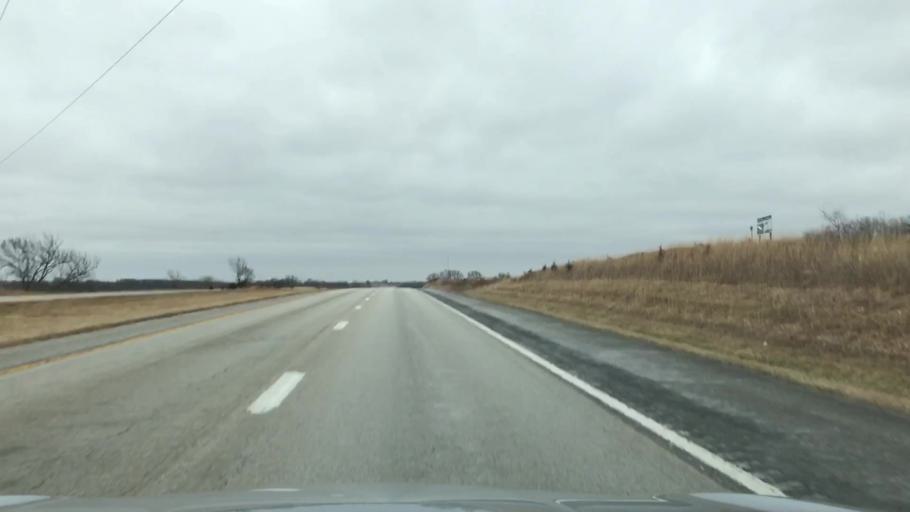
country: US
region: Missouri
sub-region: Caldwell County
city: Hamilton
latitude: 39.7495
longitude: -94.0855
